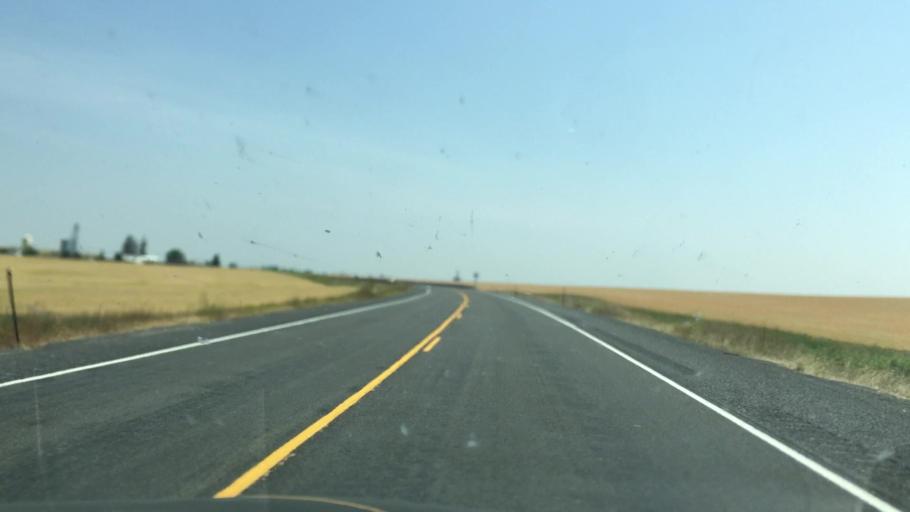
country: US
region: Idaho
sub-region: Lewis County
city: Nezperce
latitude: 46.2337
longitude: -116.5045
